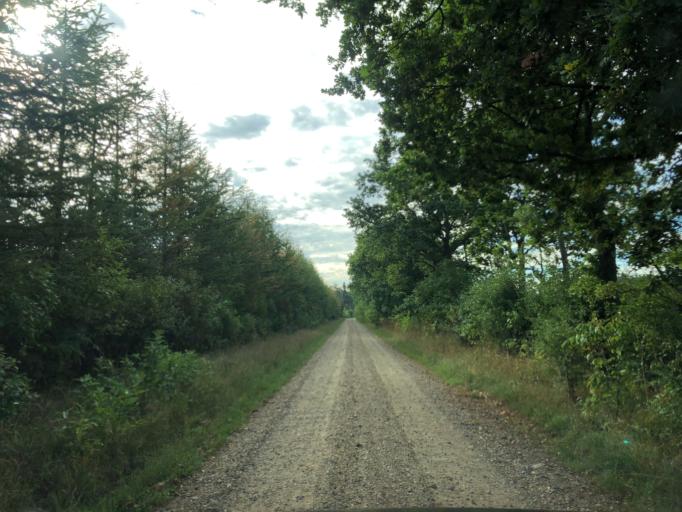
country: DK
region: Central Jutland
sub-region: Holstebro Kommune
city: Ulfborg
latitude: 56.1859
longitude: 8.3439
